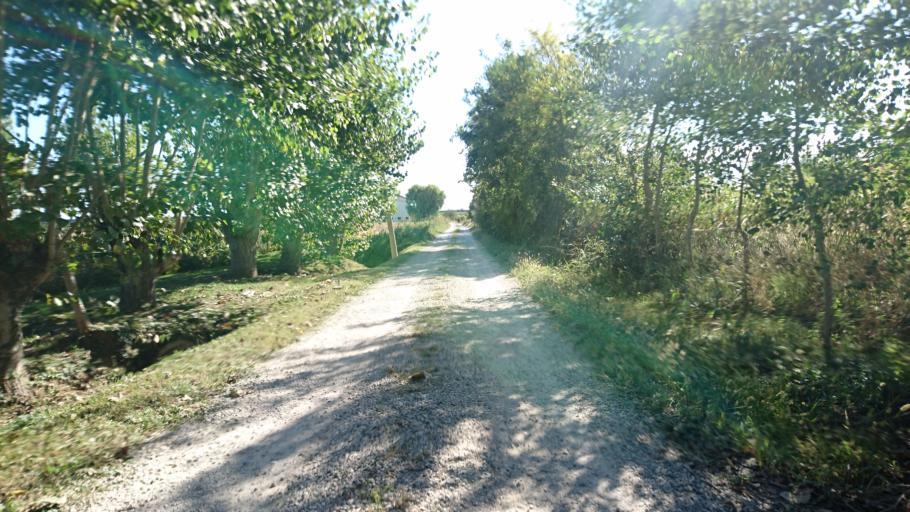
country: IT
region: Veneto
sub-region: Provincia di Padova
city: Noventa
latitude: 45.4046
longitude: 11.9600
